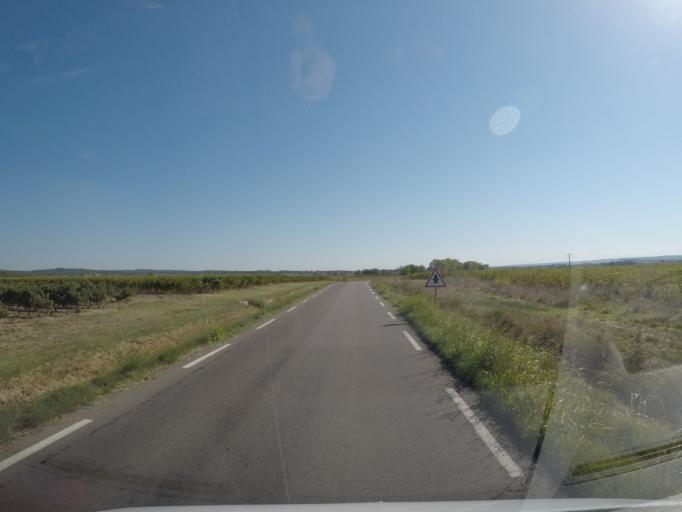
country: FR
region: Languedoc-Roussillon
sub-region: Departement du Gard
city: Moussac
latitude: 43.9837
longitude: 4.2439
